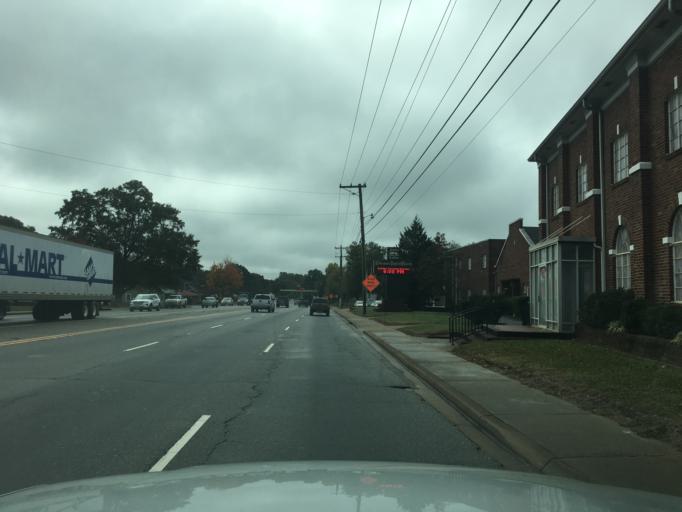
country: US
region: South Carolina
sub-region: Greenville County
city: Welcome
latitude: 34.8285
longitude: -82.4469
